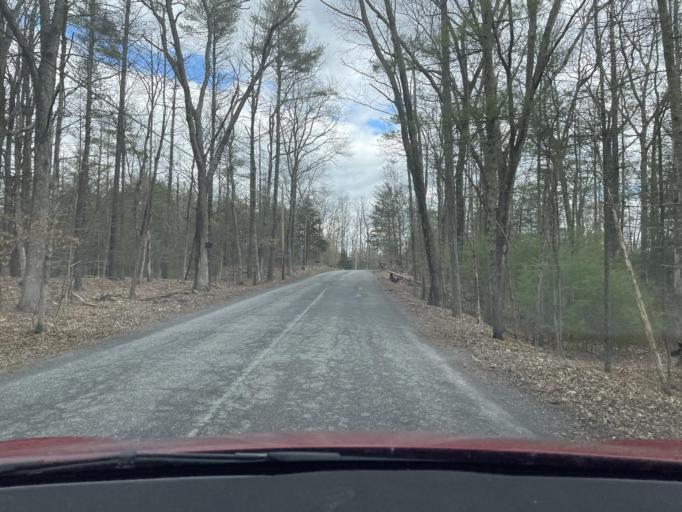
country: US
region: New York
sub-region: Ulster County
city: Zena
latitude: 42.0713
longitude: -74.0327
